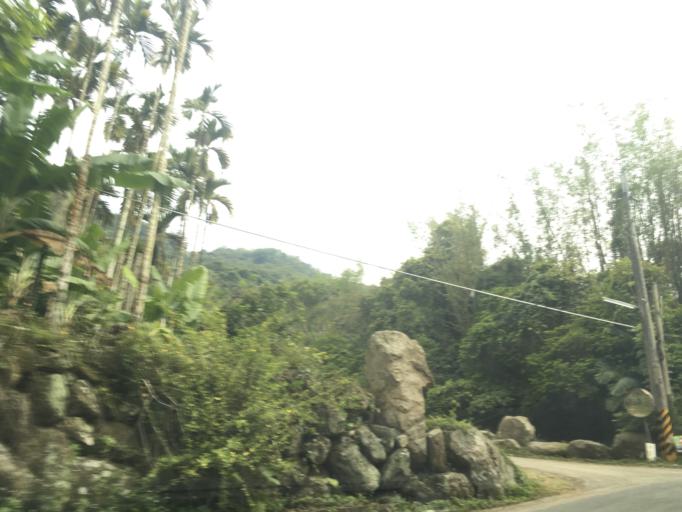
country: TW
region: Taiwan
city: Zhongxing New Village
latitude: 23.9778
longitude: 120.8204
